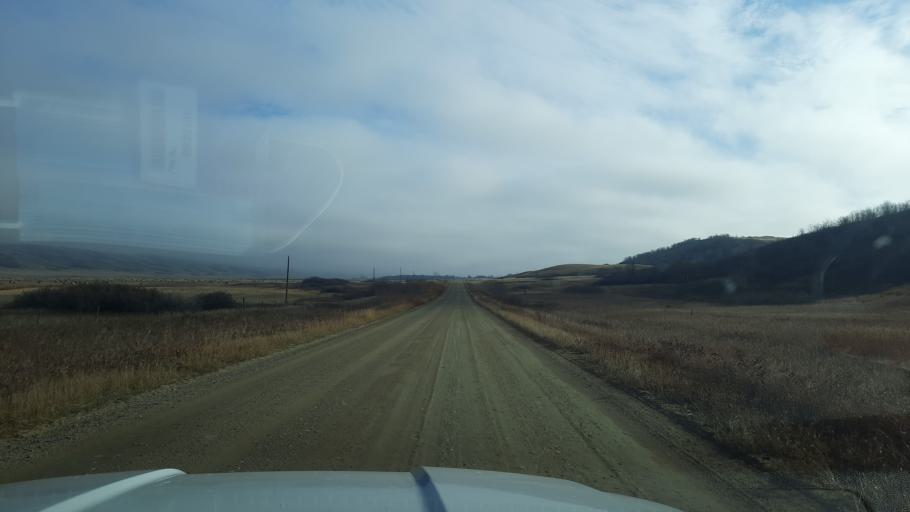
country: CA
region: Saskatchewan
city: Pilot Butte
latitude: 50.7845
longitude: -104.2051
